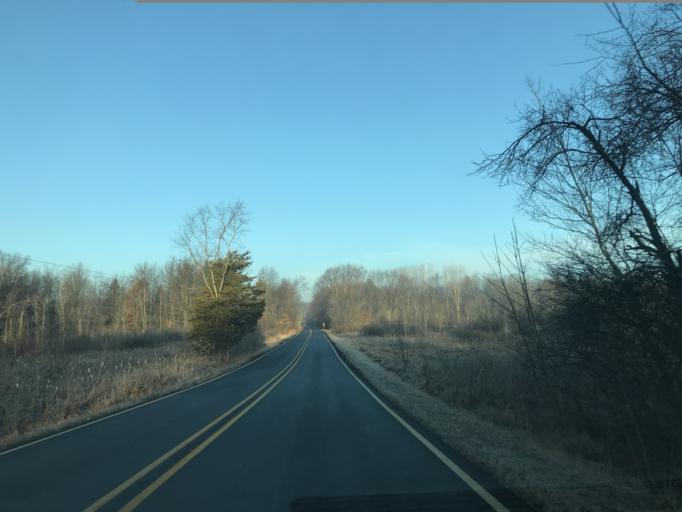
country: US
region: Michigan
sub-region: Ingham County
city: Leslie
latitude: 42.4322
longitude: -84.5340
